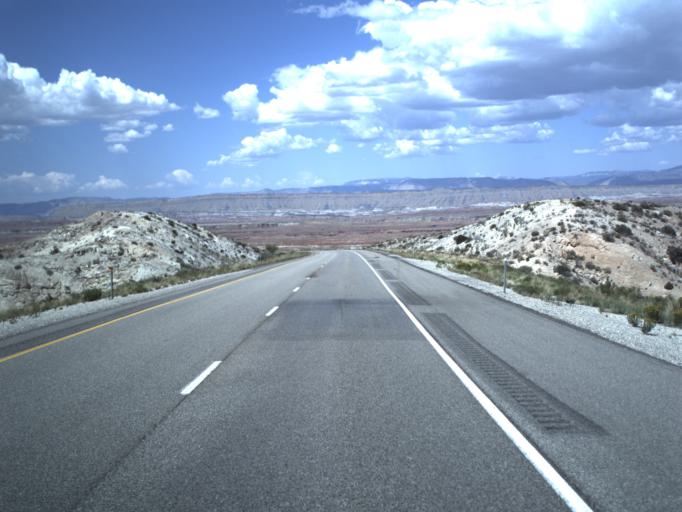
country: US
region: Utah
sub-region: Emery County
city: Ferron
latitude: 38.8451
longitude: -110.9866
